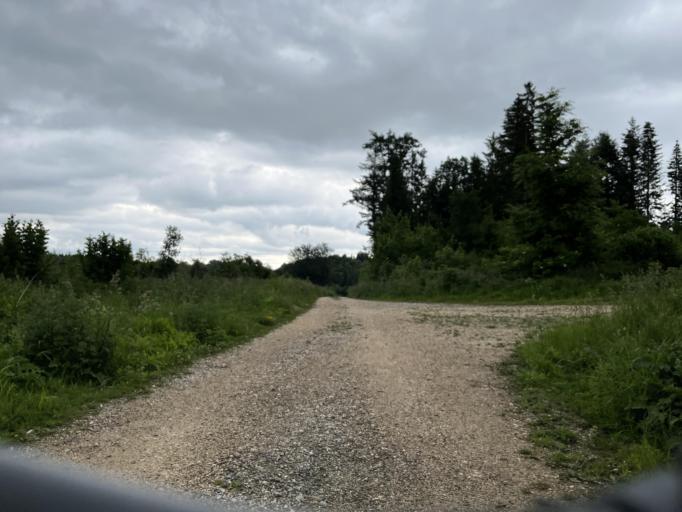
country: DE
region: Baden-Wuerttemberg
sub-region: Tuebingen Region
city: Bingen
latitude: 48.1026
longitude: 9.2513
